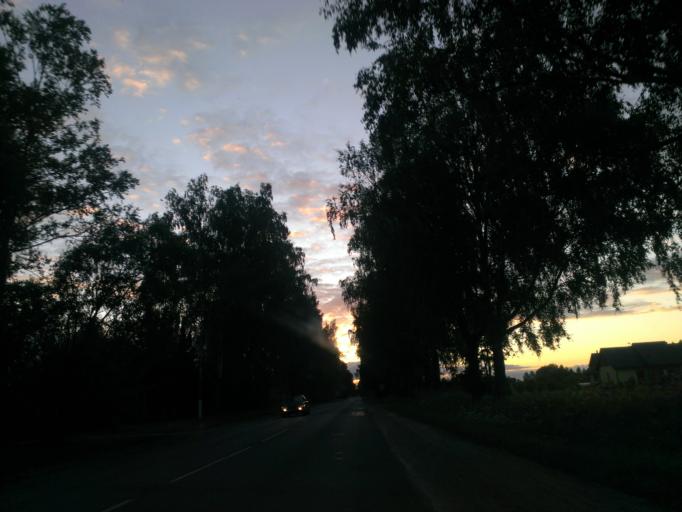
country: LV
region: Vecumnieki
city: Vecumnieki
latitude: 56.6111
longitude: 24.5138
